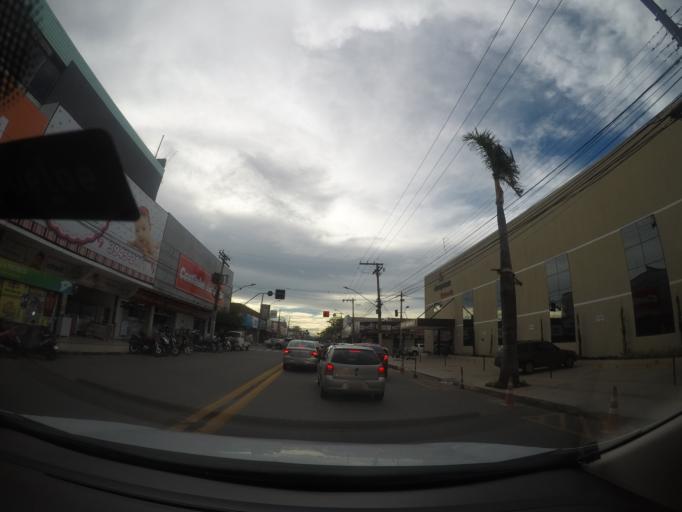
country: BR
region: Goias
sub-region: Goiania
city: Goiania
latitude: -16.6709
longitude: -49.2856
